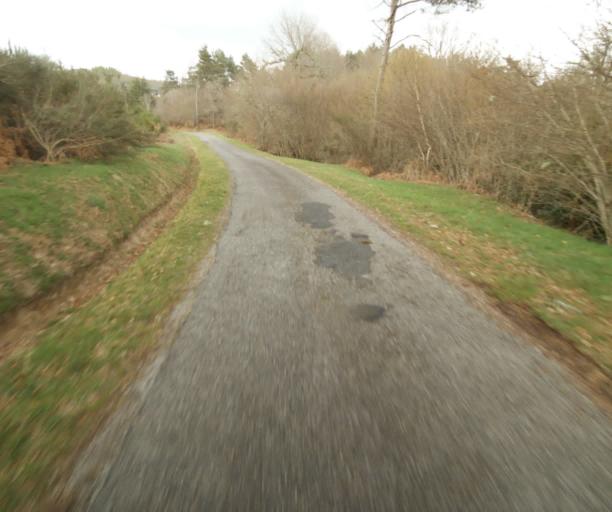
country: FR
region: Limousin
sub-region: Departement de la Correze
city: Egletons
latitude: 45.2714
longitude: 1.9965
